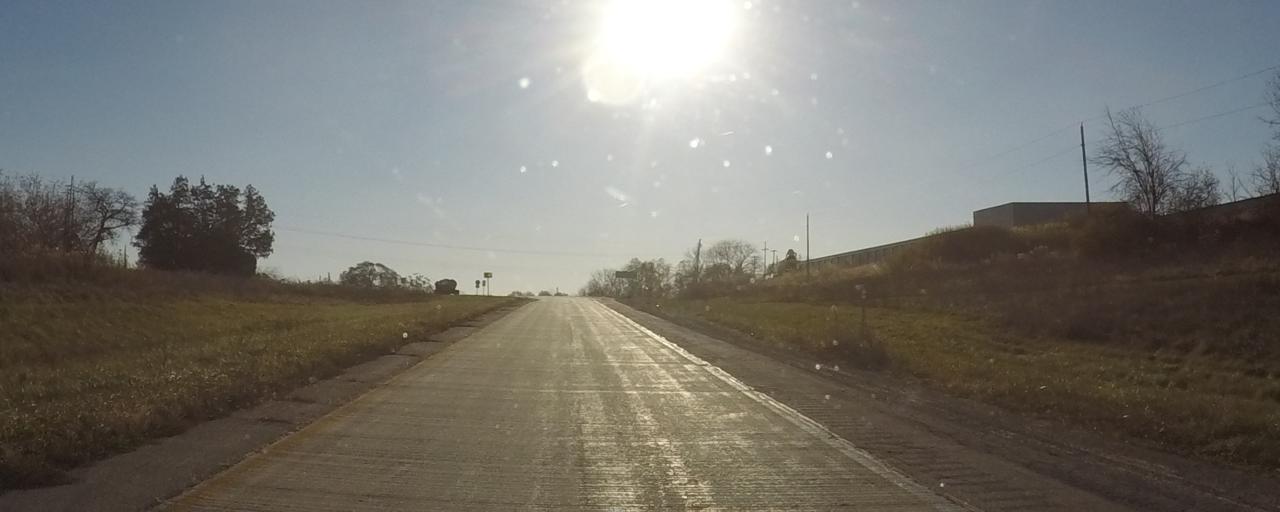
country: US
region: Wisconsin
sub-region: Dane County
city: Cottage Grove
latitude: 43.0315
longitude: -89.2025
